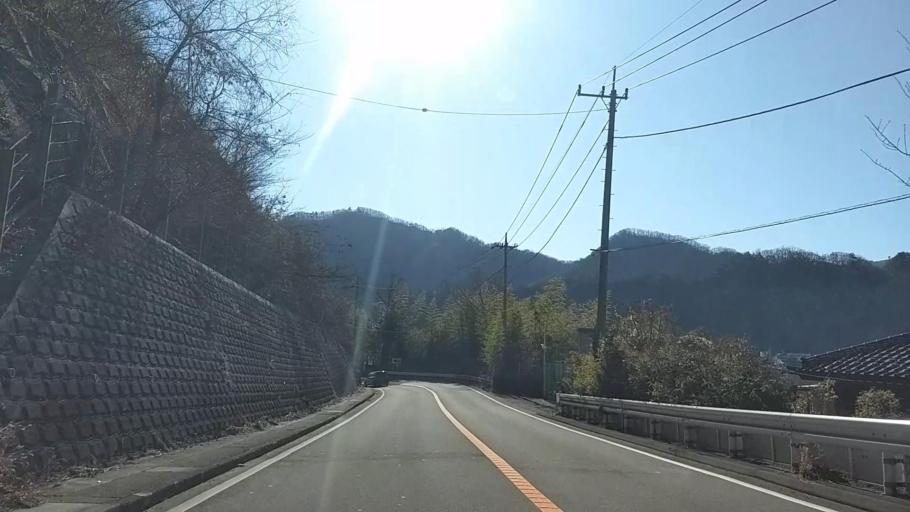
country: JP
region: Yamanashi
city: Uenohara
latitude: 35.6237
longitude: 139.1049
